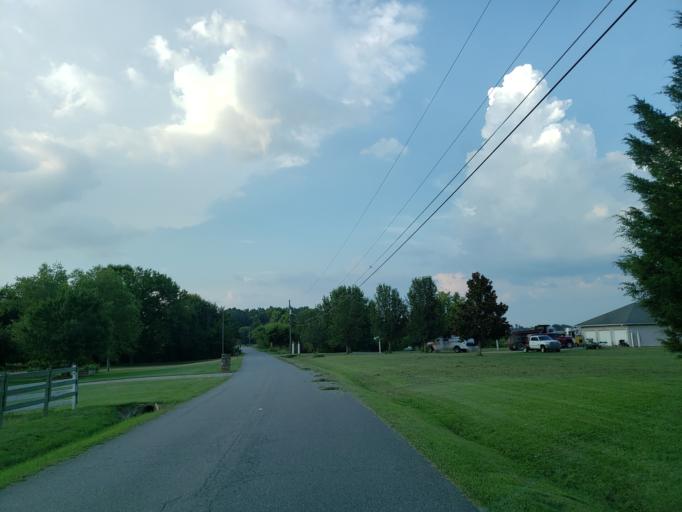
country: US
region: Georgia
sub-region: Bartow County
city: Euharlee
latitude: 34.0944
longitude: -84.9294
